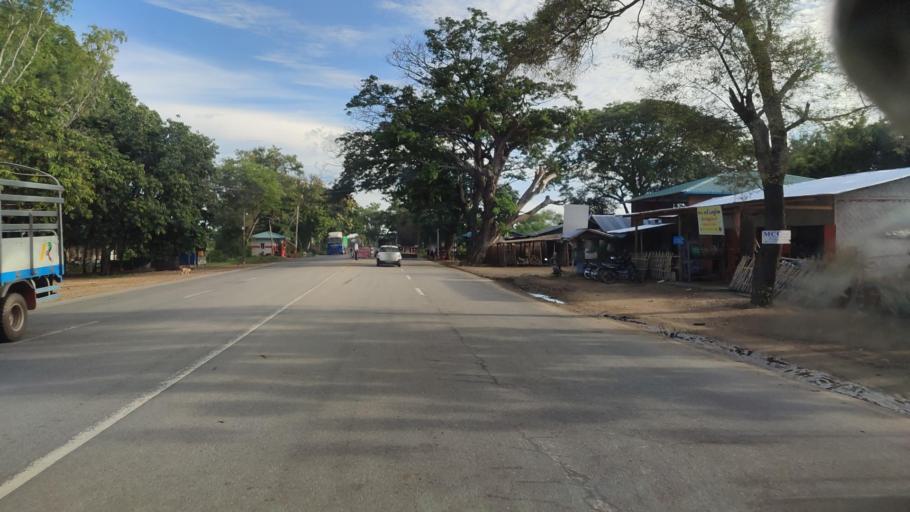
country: MM
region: Mandalay
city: Yamethin
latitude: 20.1740
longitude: 96.1889
